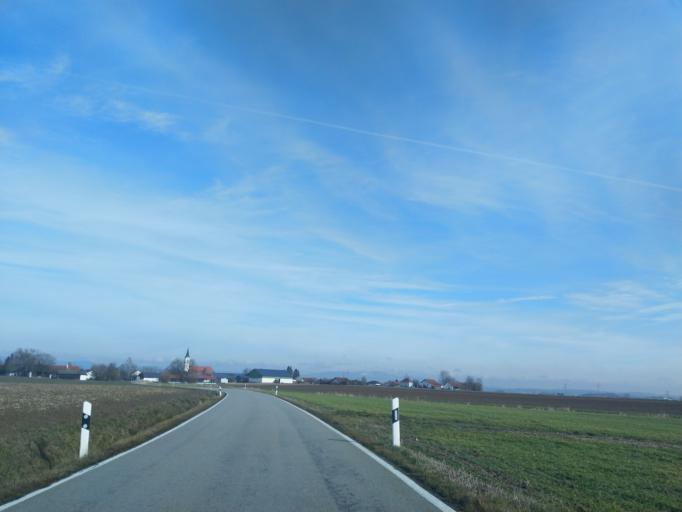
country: DE
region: Bavaria
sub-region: Lower Bavaria
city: Buchhofen
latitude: 48.6825
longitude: 12.9428
